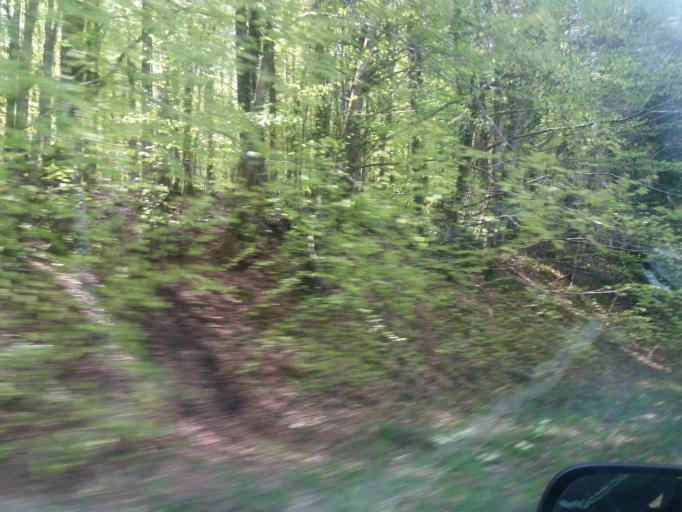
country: GB
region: Northern Ireland
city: Irvinestown
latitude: 54.4155
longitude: -7.7289
